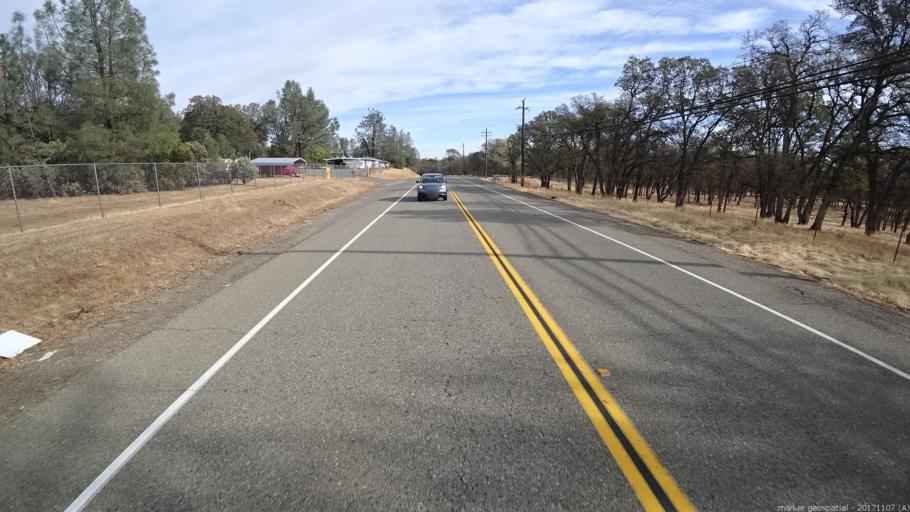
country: US
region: California
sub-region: Shasta County
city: Shasta
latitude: 40.5405
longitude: -122.4703
